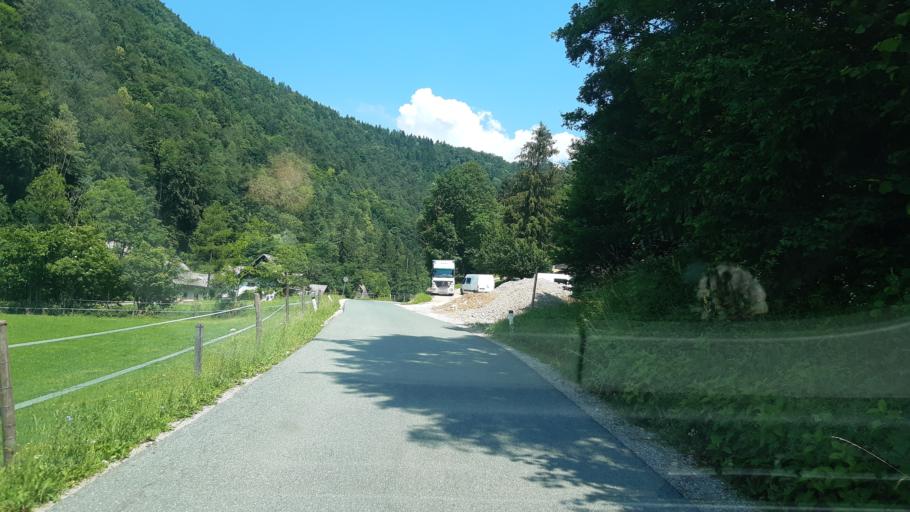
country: SI
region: Cerklje na Gorenjskem
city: Cerklje na Gorenjskem
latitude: 46.2667
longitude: 14.4938
